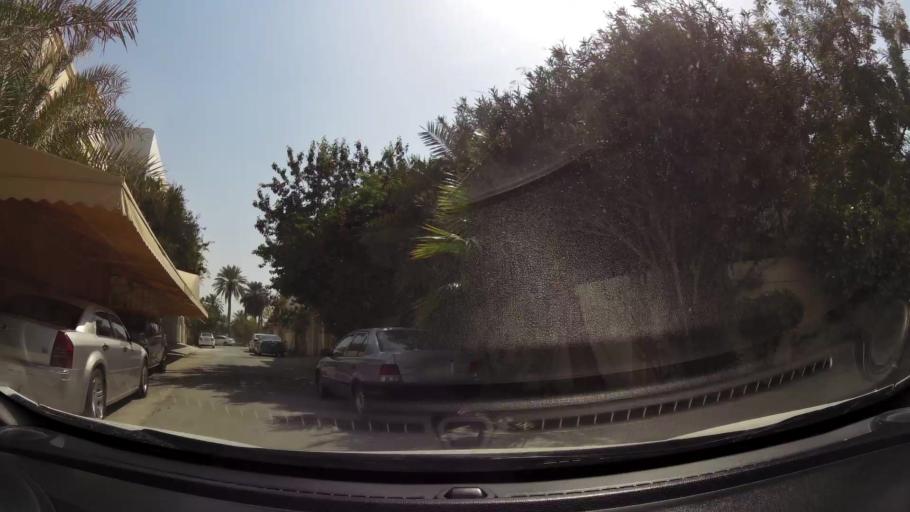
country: BH
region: Manama
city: Jidd Hafs
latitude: 26.2068
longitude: 50.4563
